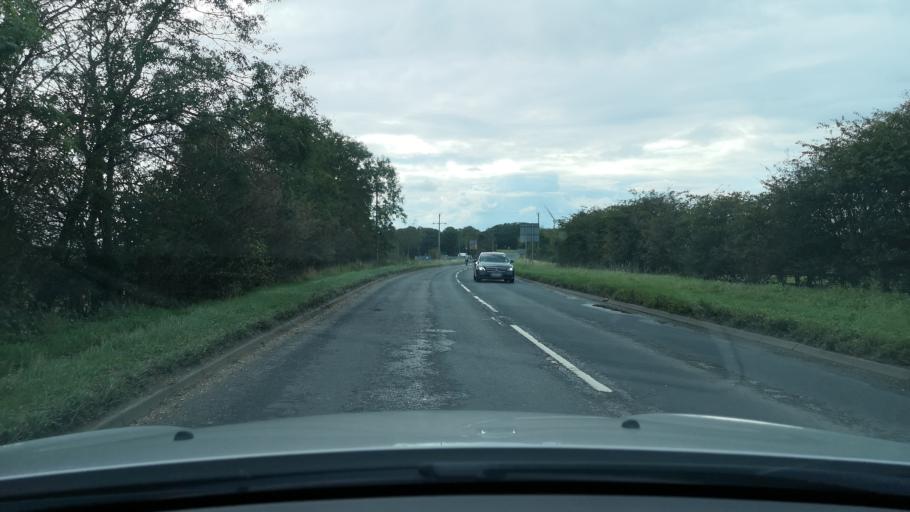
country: GB
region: England
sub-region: East Riding of Yorkshire
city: North Cave
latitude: 53.7729
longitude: -0.6706
